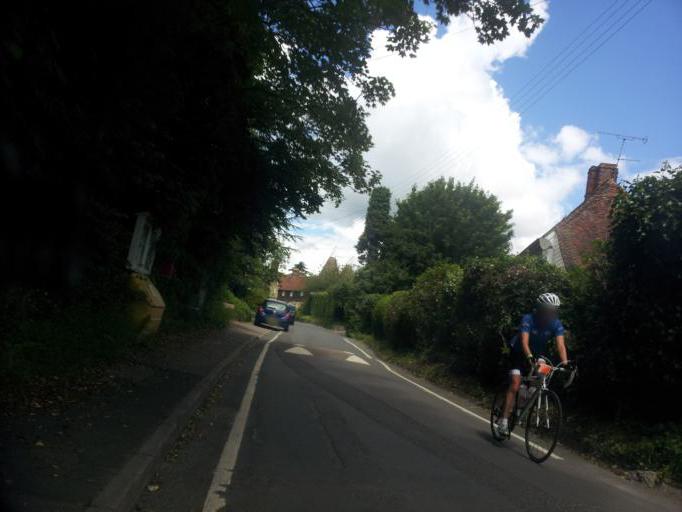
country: GB
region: England
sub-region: Kent
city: Meopham
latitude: 51.3154
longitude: 0.3535
